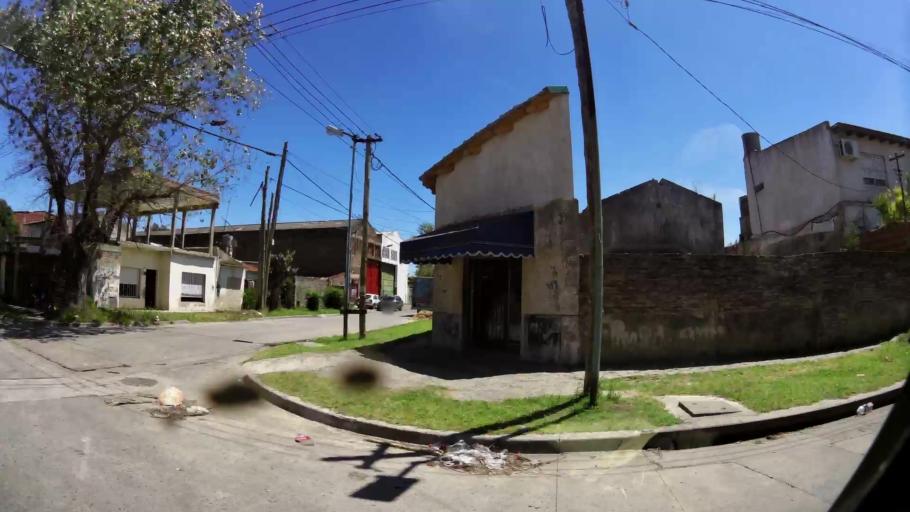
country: AR
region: Buenos Aires
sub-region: Partido de Quilmes
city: Quilmes
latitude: -34.7180
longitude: -58.3125
